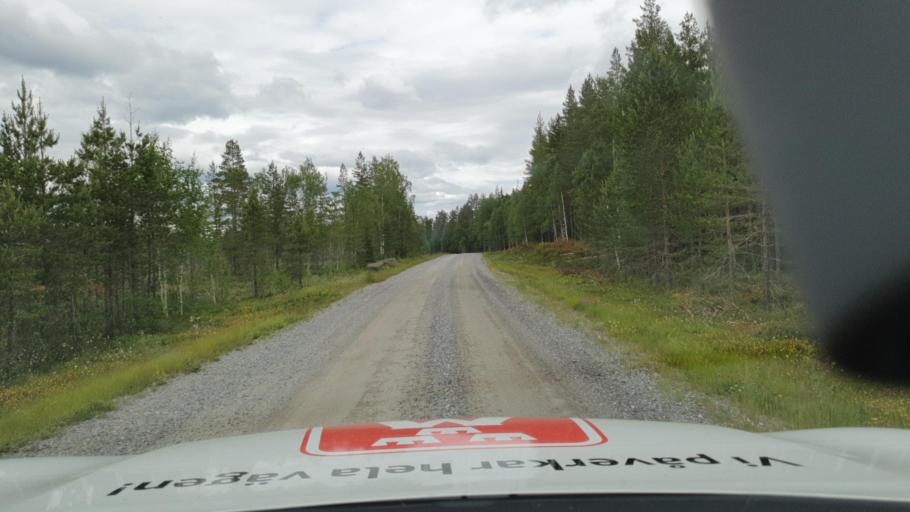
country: SE
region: Vaesterbotten
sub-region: Nordmalings Kommun
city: Nordmaling
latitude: 63.7194
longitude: 19.4288
